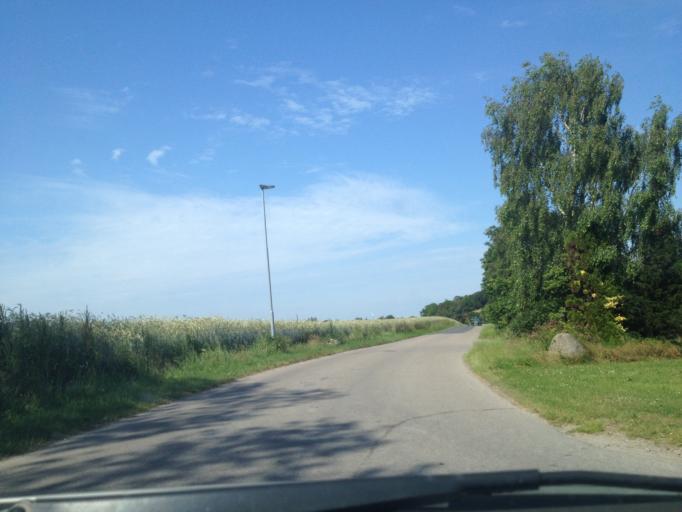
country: DK
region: Central Jutland
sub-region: Samso Kommune
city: Tranebjerg
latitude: 55.8403
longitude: 10.5563
